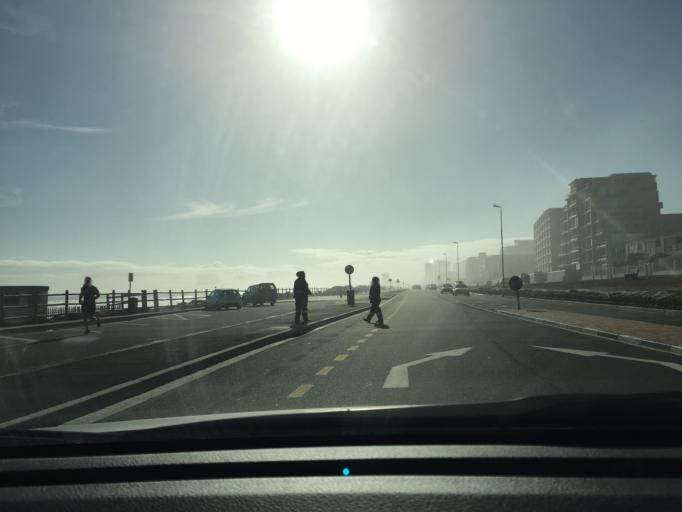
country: ZA
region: Western Cape
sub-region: City of Cape Town
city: Sunset Beach
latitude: -33.8202
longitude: 18.4755
